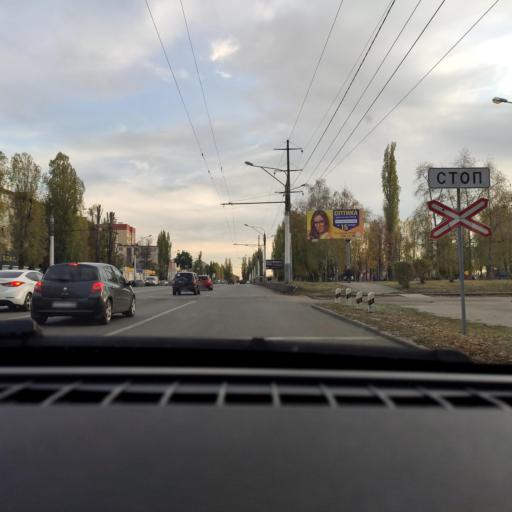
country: RU
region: Voronezj
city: Maslovka
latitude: 51.6066
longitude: 39.2370
